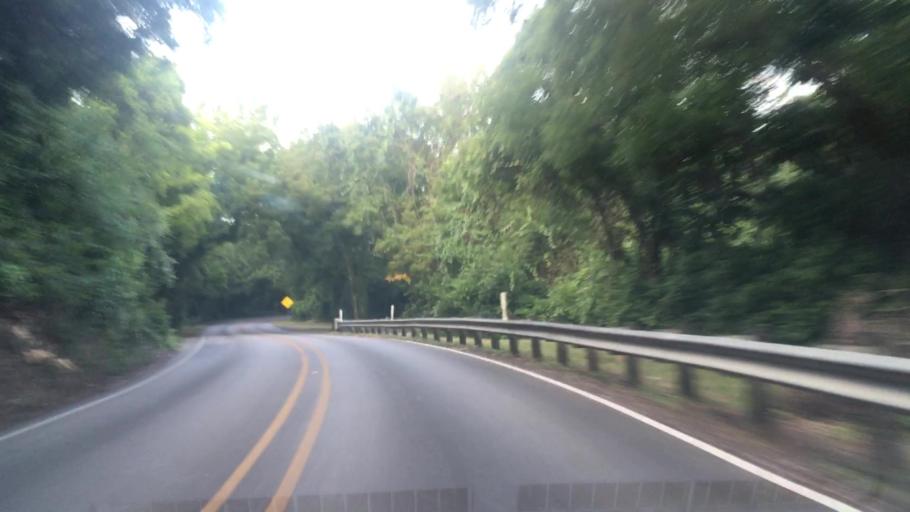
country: US
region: Texas
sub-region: Williamson County
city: Anderson Mill
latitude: 30.4482
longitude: -97.8580
